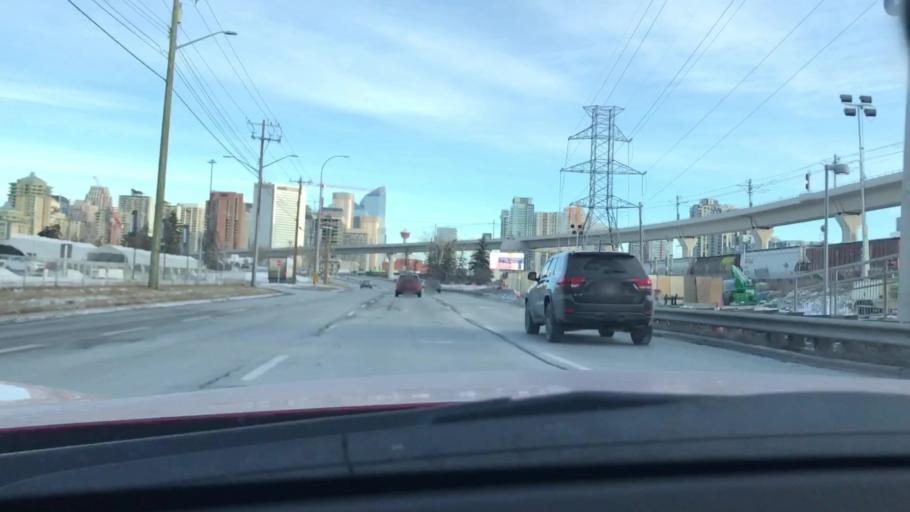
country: CA
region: Alberta
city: Calgary
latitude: 51.0453
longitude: -114.0985
